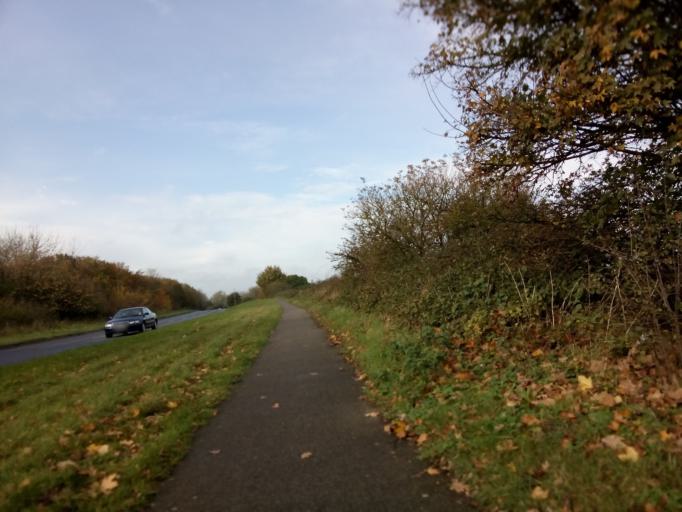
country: GB
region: England
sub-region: Suffolk
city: Needham Market
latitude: 52.1660
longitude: 1.0332
